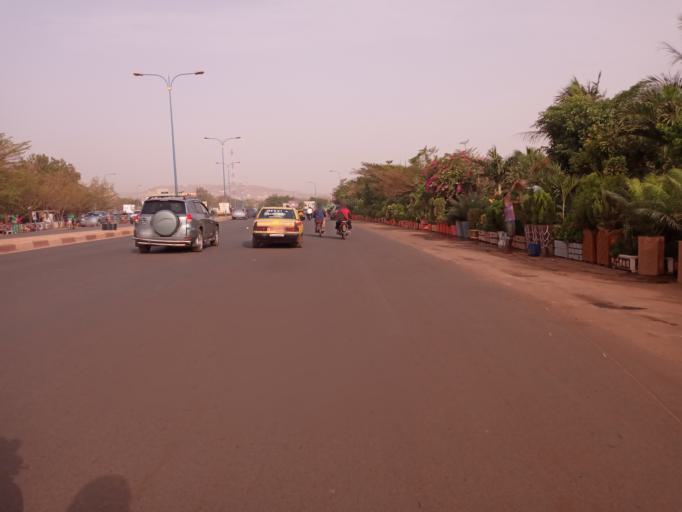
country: ML
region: Bamako
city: Bamako
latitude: 12.6361
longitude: -8.0153
